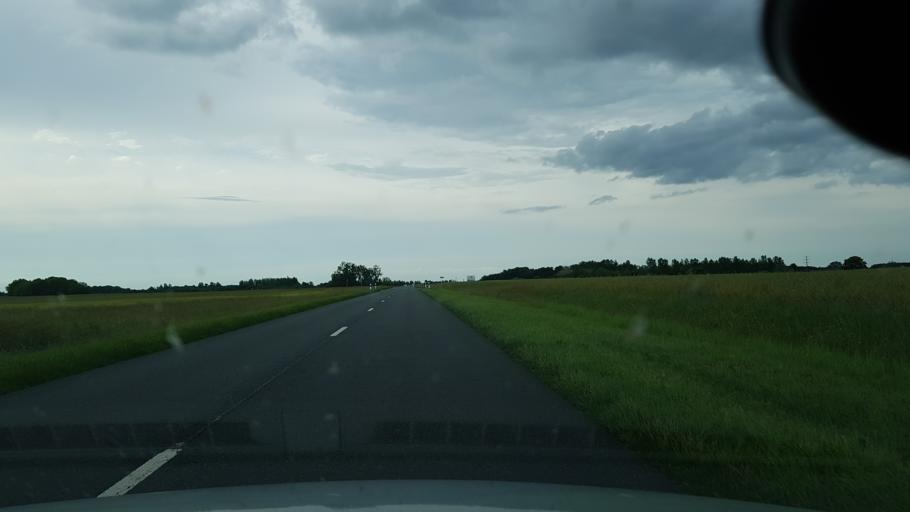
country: FR
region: Centre
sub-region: Departement du Loir-et-Cher
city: Chatillon-sur-Cher
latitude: 47.3114
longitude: 1.5034
